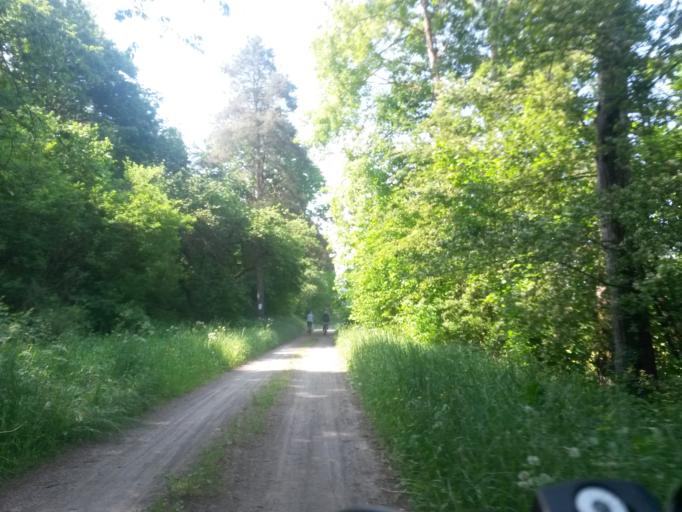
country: DE
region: Bavaria
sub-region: Regierungsbezirk Unterfranken
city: Euerdorf
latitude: 50.1580
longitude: 10.0380
